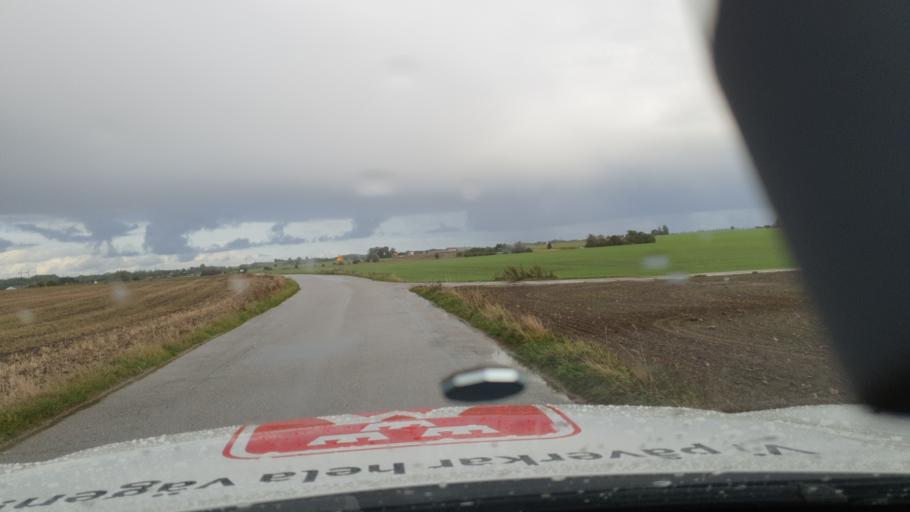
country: SE
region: Skane
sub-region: Malmo
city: Tygelsjo
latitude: 55.5174
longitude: 13.0359
